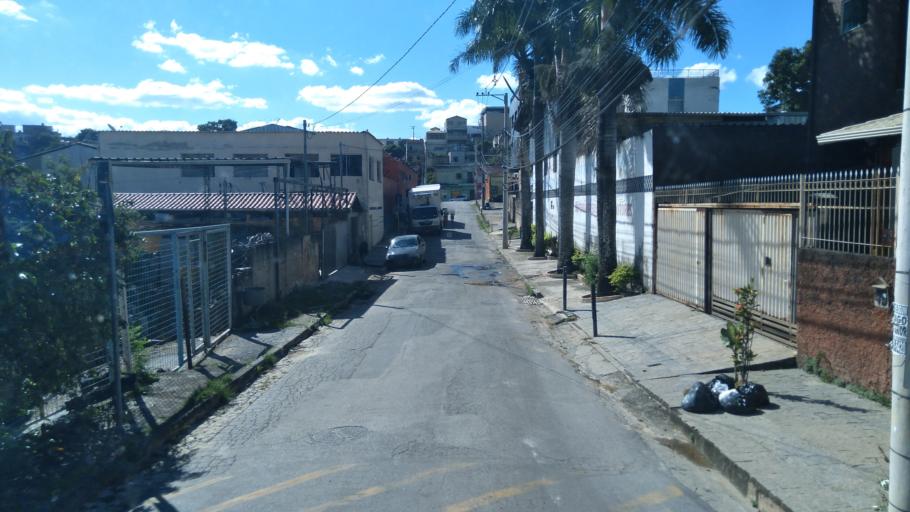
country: BR
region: Minas Gerais
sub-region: Belo Horizonte
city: Belo Horizonte
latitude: -19.8536
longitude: -43.8881
